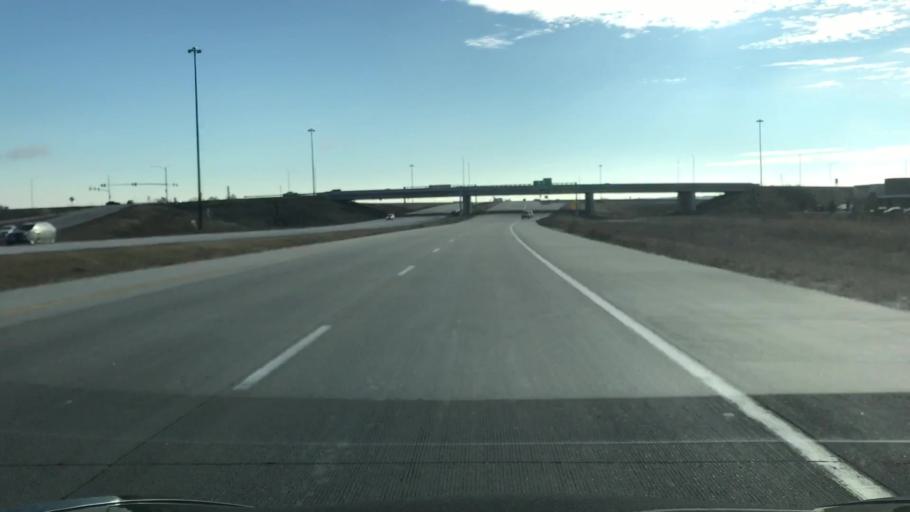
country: US
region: Iowa
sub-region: Pottawattamie County
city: Council Bluffs
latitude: 41.2229
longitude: -95.8345
